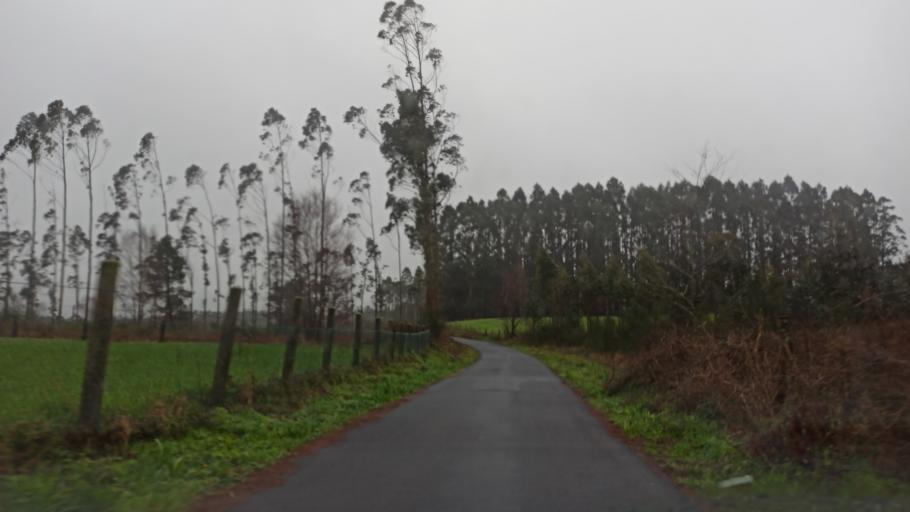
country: ES
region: Galicia
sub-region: Provincia da Coruna
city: Coiros
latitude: 43.1842
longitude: -8.1248
